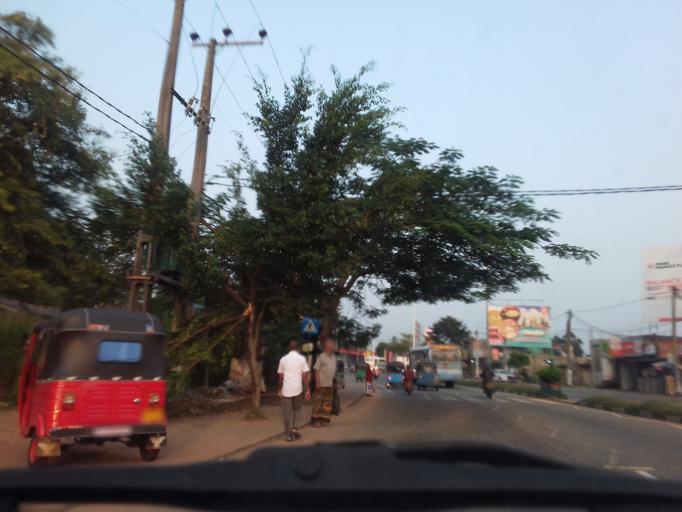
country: LK
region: Western
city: Kelaniya
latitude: 6.9911
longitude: 79.9402
